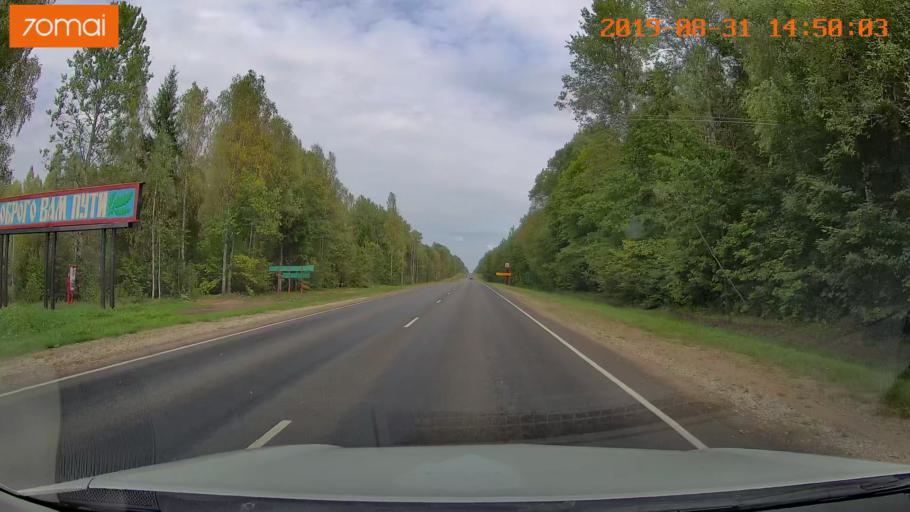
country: RU
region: Kaluga
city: Spas-Demensk
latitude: 54.2585
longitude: 33.7800
